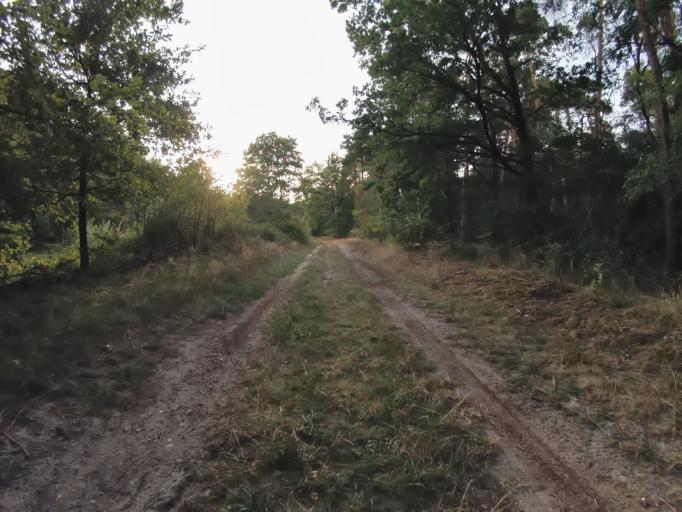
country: DE
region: Lower Saxony
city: Neuenkirchen
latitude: 52.3724
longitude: 7.8768
